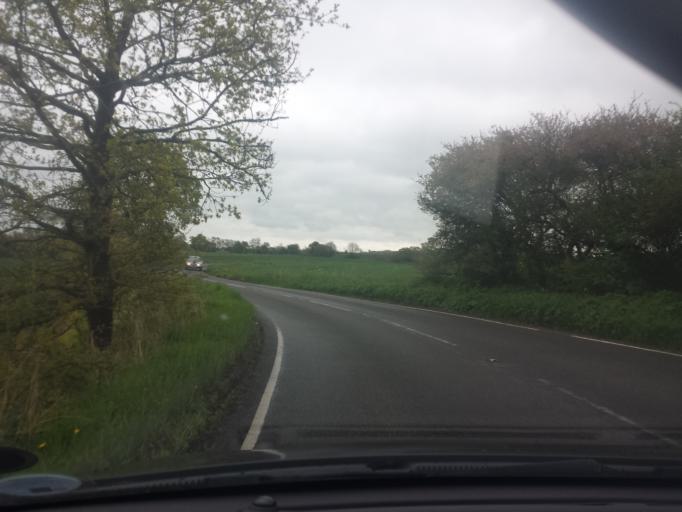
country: GB
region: England
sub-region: Essex
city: Mistley
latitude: 51.9400
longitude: 1.1020
